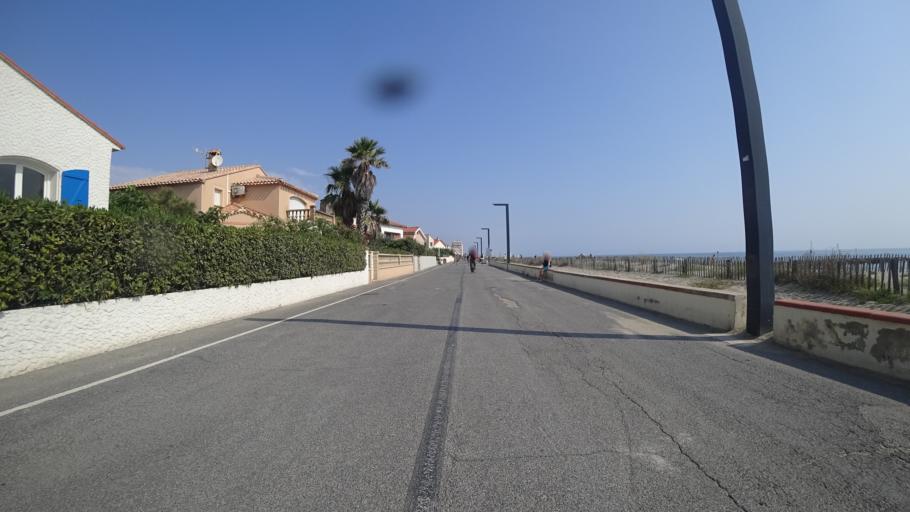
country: FR
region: Languedoc-Roussillon
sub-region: Departement des Pyrenees-Orientales
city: Saint-Cyprien-Plage
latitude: 42.6255
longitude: 3.0362
